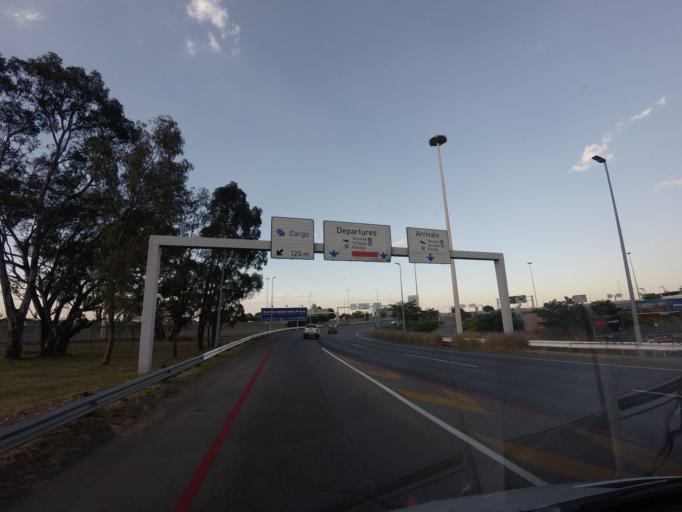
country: ZA
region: Gauteng
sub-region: City of Johannesburg Metropolitan Municipality
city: Modderfontein
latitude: -26.1305
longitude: 28.2291
